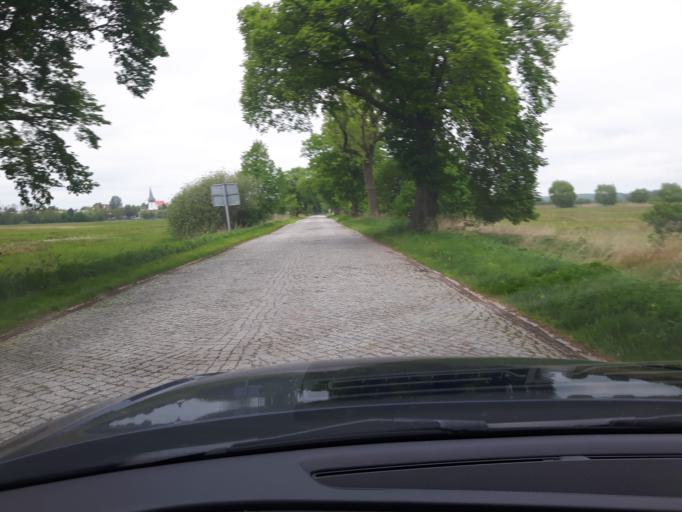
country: DE
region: Mecklenburg-Vorpommern
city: Bad Sulze
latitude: 54.1030
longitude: 12.6744
